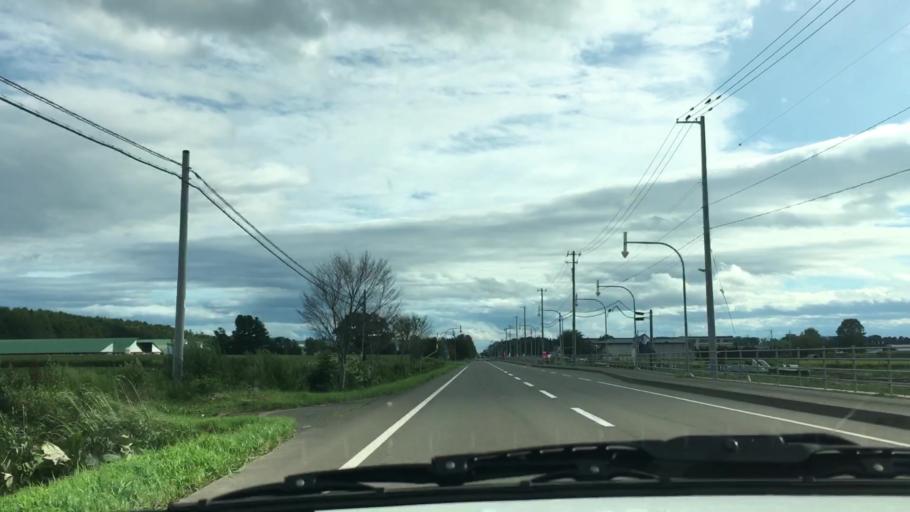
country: JP
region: Hokkaido
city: Otofuke
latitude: 43.2556
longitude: 143.3002
